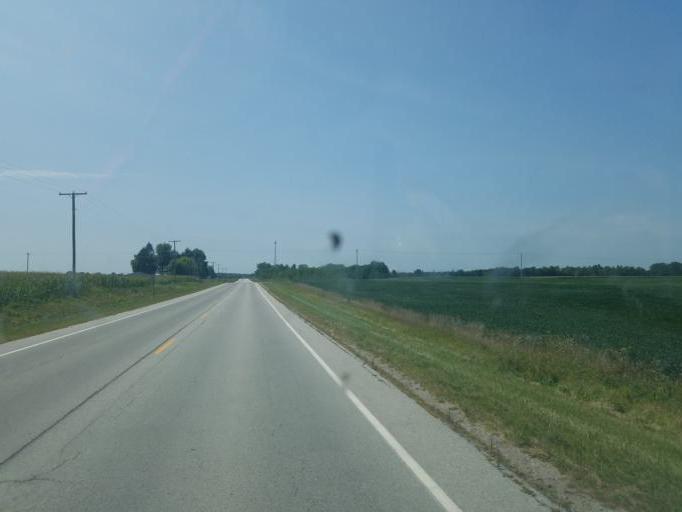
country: US
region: Ohio
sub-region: Crawford County
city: Bucyrus
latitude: 40.8436
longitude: -83.1101
